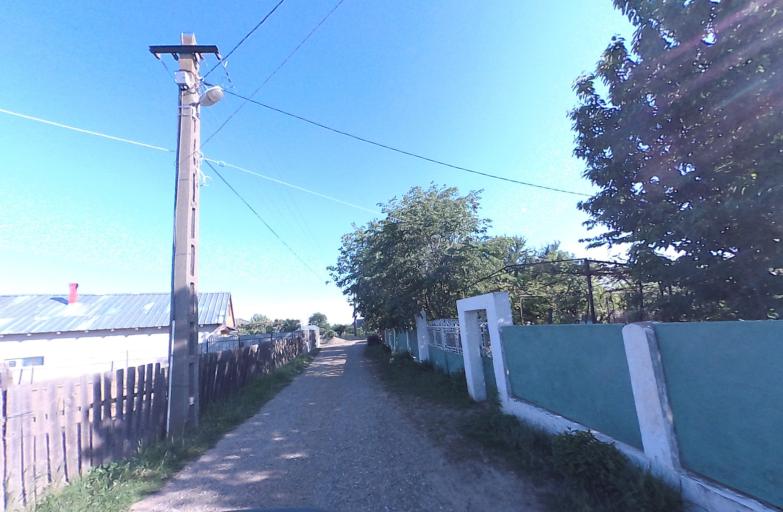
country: RO
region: Neamt
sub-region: Comuna Cordun
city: Pildesti
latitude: 46.9845
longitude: 26.8043
